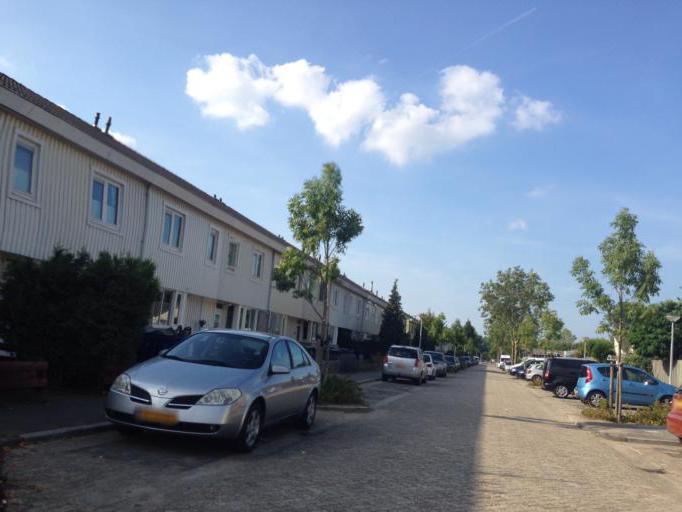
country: NL
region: Flevoland
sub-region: Gemeente Almere
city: Almere Stad
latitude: 52.3963
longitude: 5.2632
